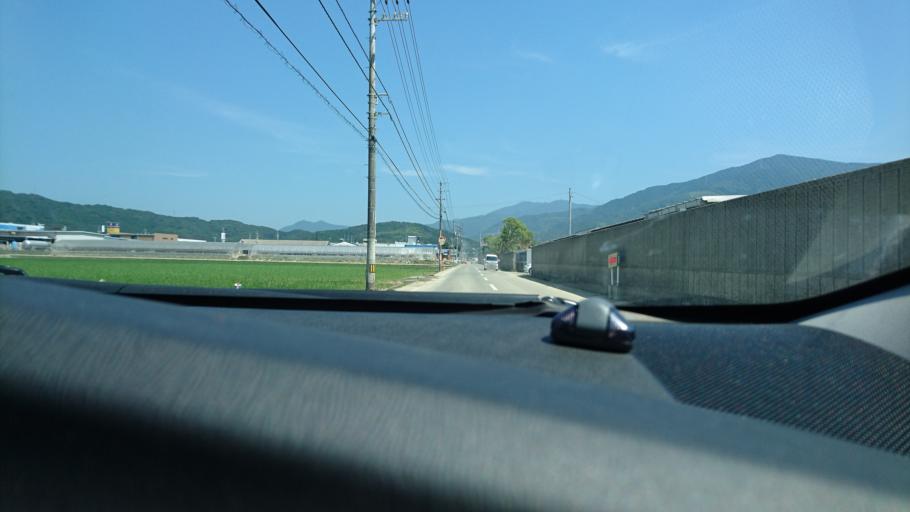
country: JP
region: Ehime
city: Ozu
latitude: 33.5261
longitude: 132.5699
